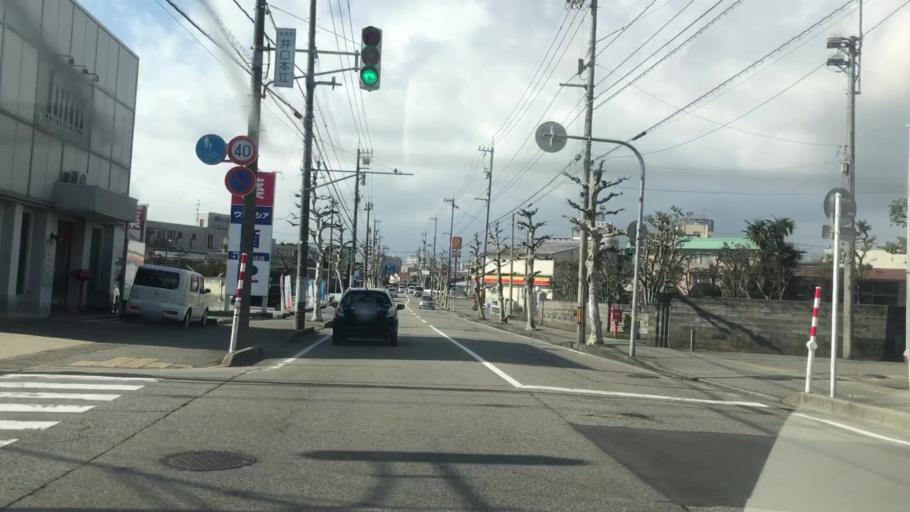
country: JP
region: Toyama
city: Takaoka
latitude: 36.7377
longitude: 137.0293
